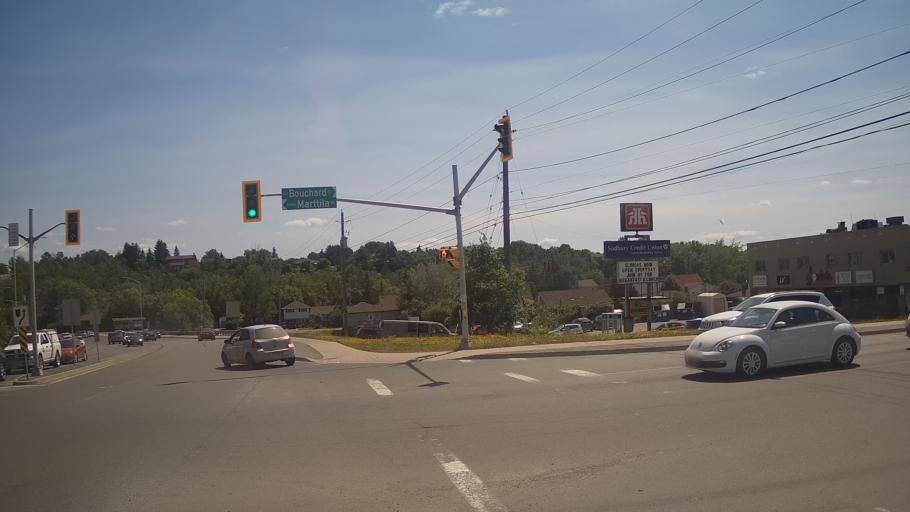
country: CA
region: Ontario
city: Greater Sudbury
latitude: 46.4613
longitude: -81.0107
